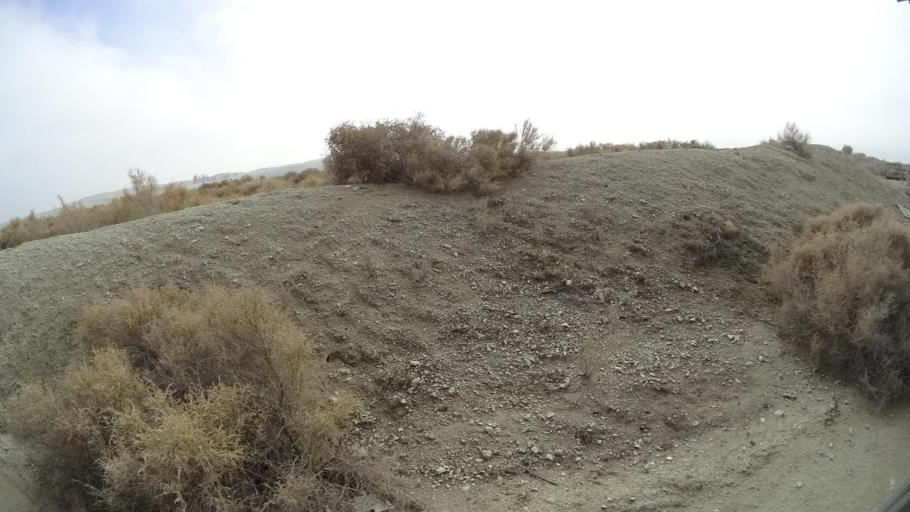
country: US
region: California
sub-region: Kern County
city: Maricopa
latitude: 35.0472
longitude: -119.3637
